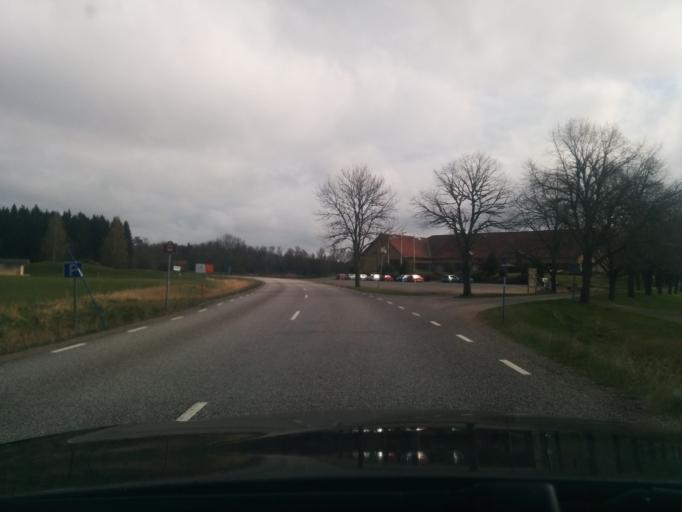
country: SE
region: Uppsala
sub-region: Tierps Kommun
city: Orbyhus
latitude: 60.1991
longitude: 17.6988
